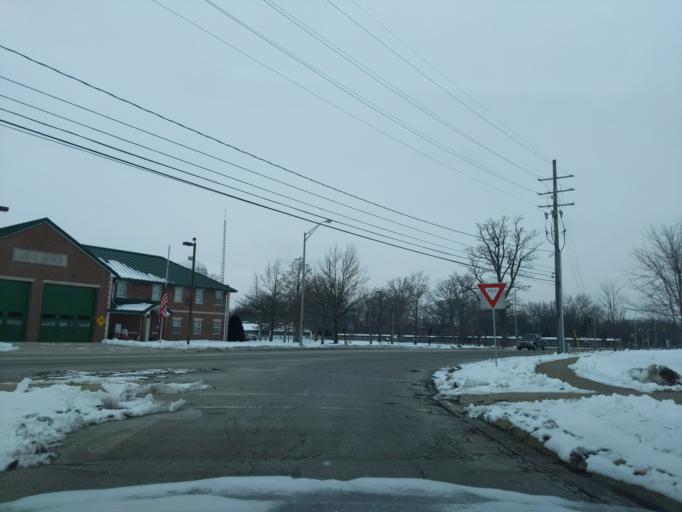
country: US
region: Indiana
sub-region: Tippecanoe County
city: Lafayette
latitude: 40.3956
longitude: -86.8761
